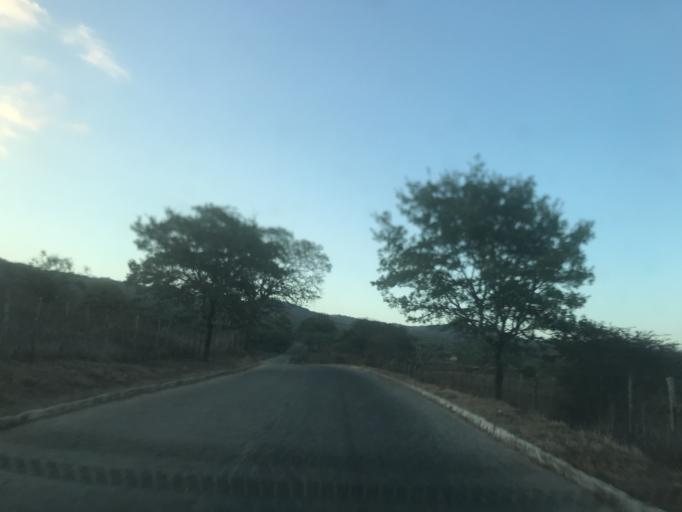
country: BR
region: Pernambuco
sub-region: Bezerros
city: Bezerros
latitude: -8.2065
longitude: -35.7583
